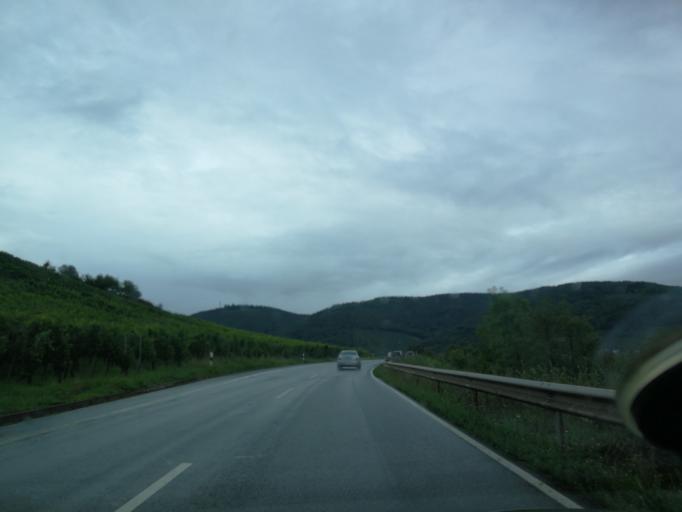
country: DE
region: Rheinland-Pfalz
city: Lieser
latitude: 49.9136
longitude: 7.0408
